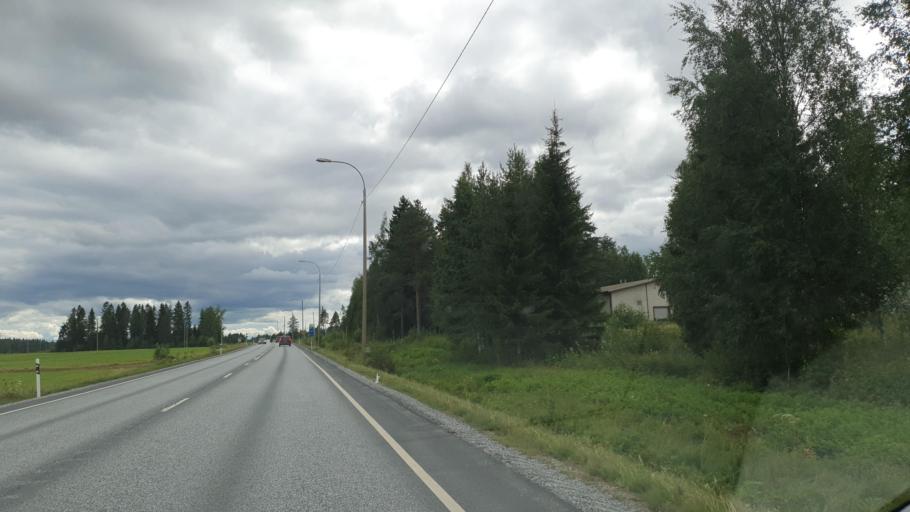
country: FI
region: Northern Savo
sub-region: Ylae-Savo
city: Sonkajaervi
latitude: 63.8724
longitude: 27.4402
